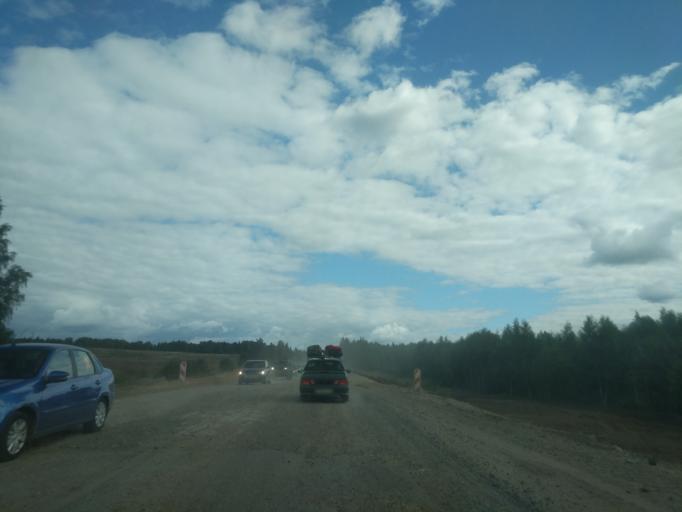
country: RU
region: Kostroma
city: Sudislavl'
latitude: 57.8729
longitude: 41.7396
